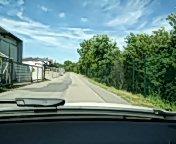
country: DE
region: Baden-Wuerttemberg
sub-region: Karlsruhe Region
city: Mosbach
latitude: 49.3833
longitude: 9.1837
